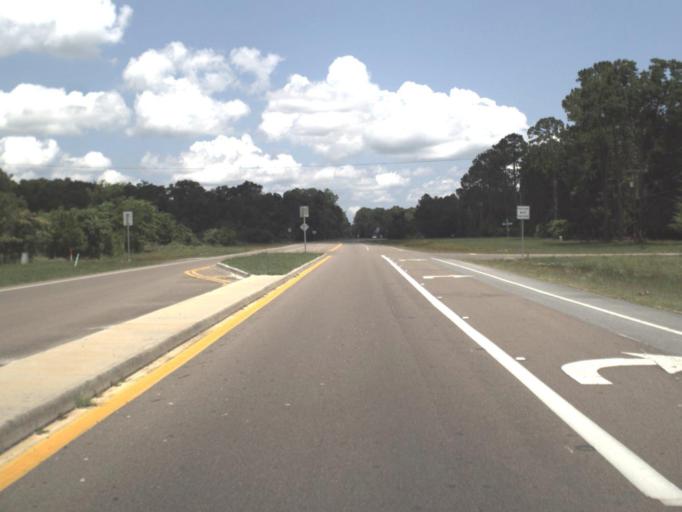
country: US
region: Florida
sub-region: Alachua County
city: High Springs
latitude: 29.8413
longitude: -82.6040
